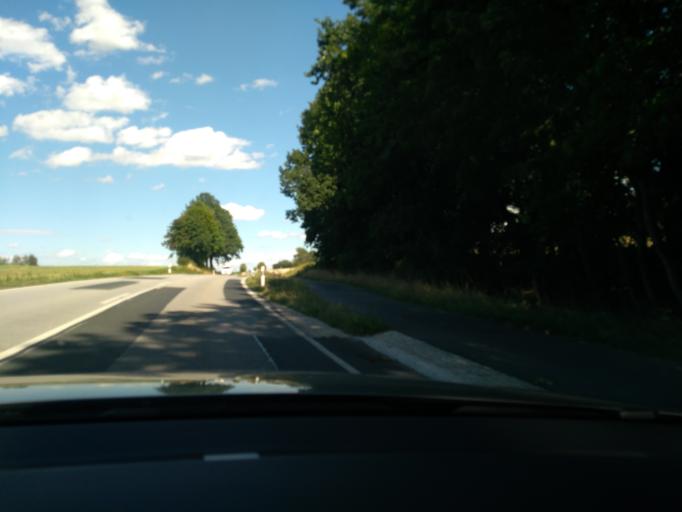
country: DE
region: Saxony
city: Goda
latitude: 51.1680
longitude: 14.2841
